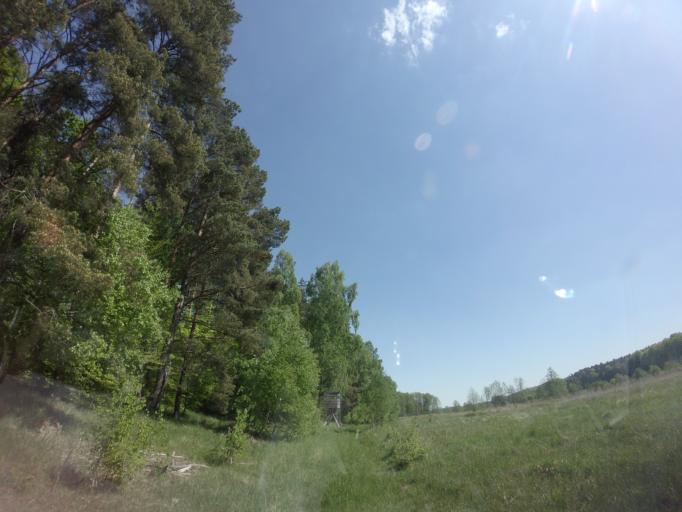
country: PL
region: West Pomeranian Voivodeship
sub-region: Powiat choszczenski
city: Pelczyce
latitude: 52.9498
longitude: 15.3298
